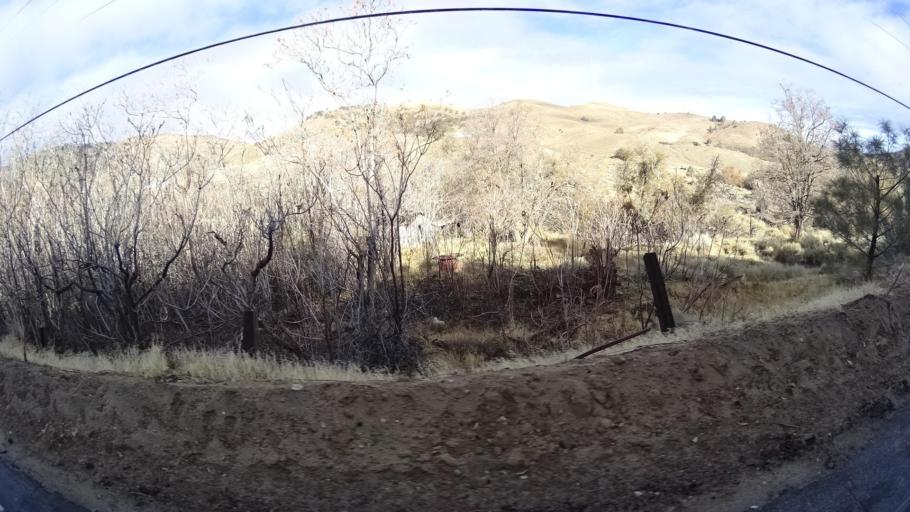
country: US
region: California
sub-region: Kern County
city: Tehachapi
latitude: 35.0789
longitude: -118.3321
